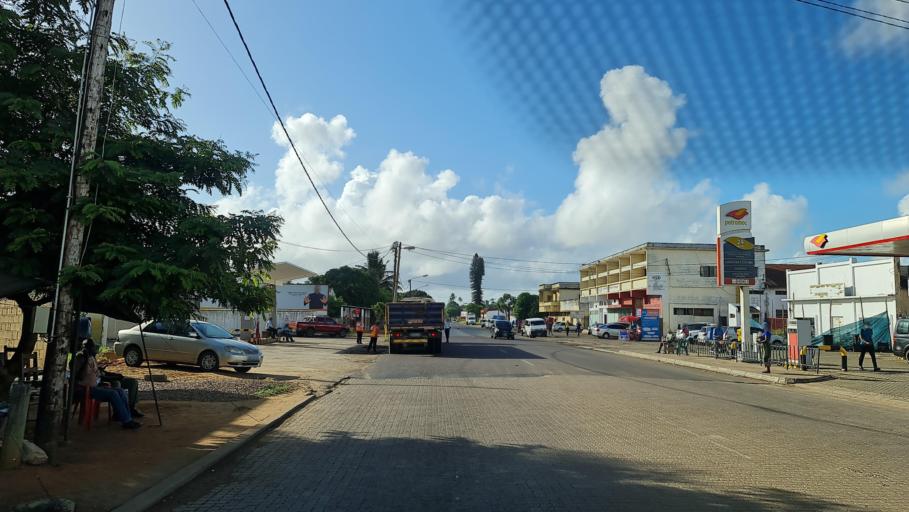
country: MZ
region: Gaza
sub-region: Xai-Xai District
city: Xai-Xai
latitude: -25.0292
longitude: 33.6325
